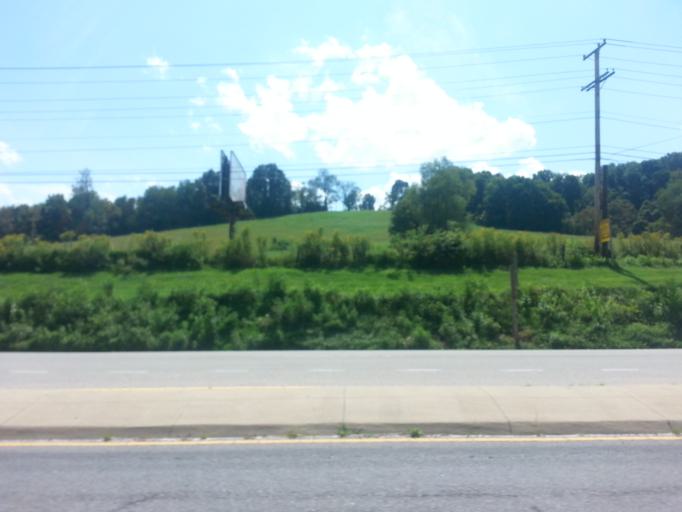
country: US
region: Virginia
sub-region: Washington County
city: Abingdon
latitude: 36.7139
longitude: -81.9995
